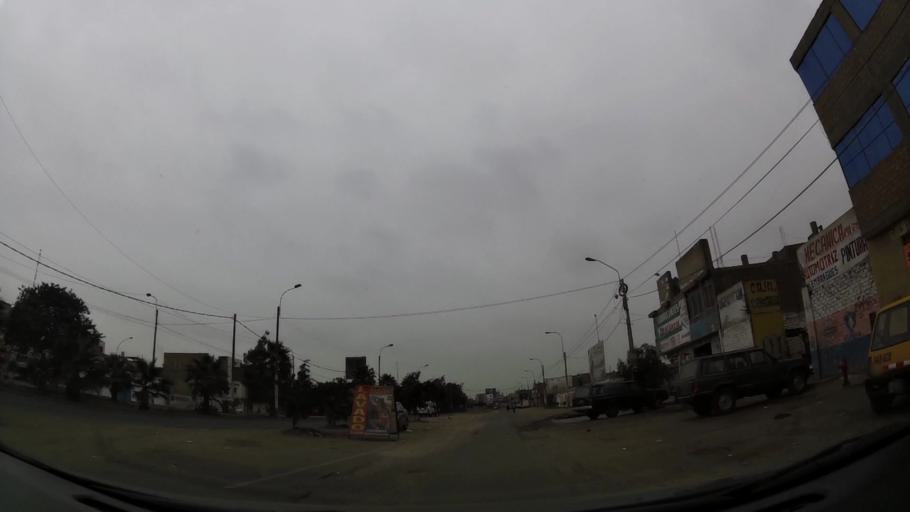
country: PE
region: Lima
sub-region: Lima
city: Independencia
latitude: -11.9590
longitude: -77.0606
